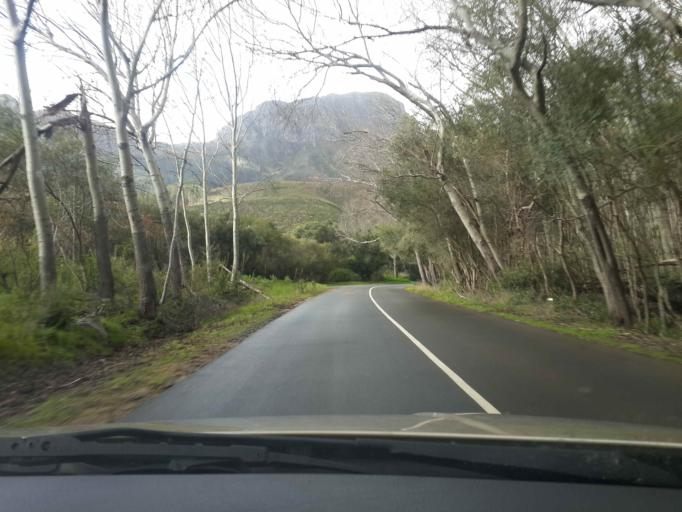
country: ZA
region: Western Cape
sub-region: Cape Winelands District Municipality
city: Stellenbosch
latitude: -33.9655
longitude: 18.9293
